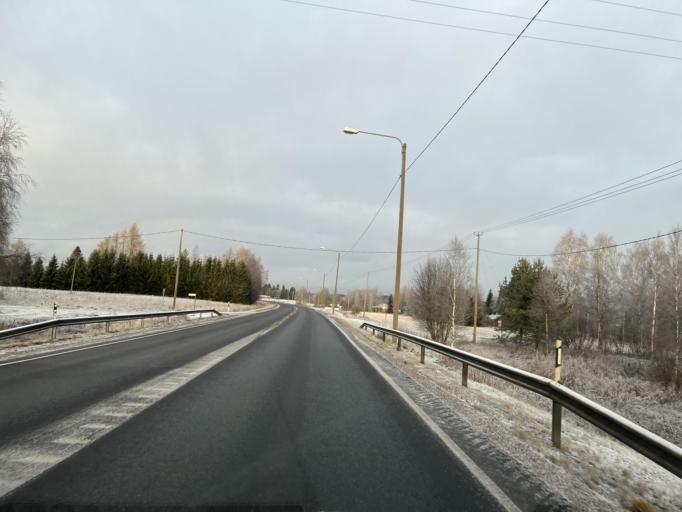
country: FI
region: Northern Ostrobothnia
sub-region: Oulu
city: Muhos
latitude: 64.8568
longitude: 25.8941
